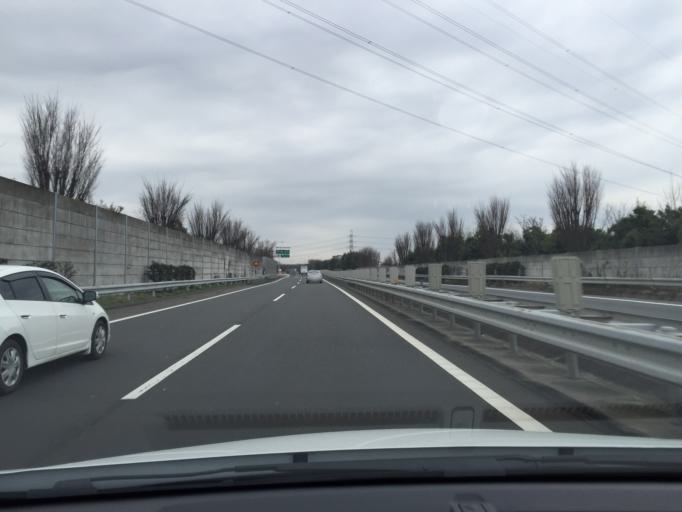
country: JP
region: Saitama
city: Sakado
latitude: 35.9238
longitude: 139.3916
